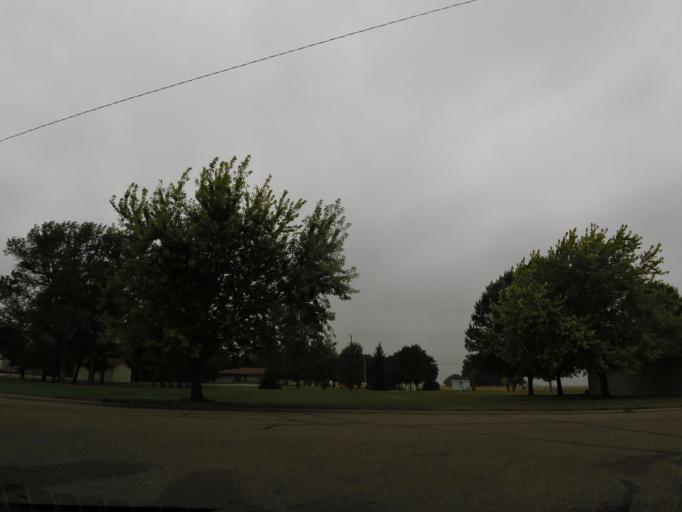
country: US
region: Minnesota
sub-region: Marshall County
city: Warren
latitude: 48.3338
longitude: -96.8256
